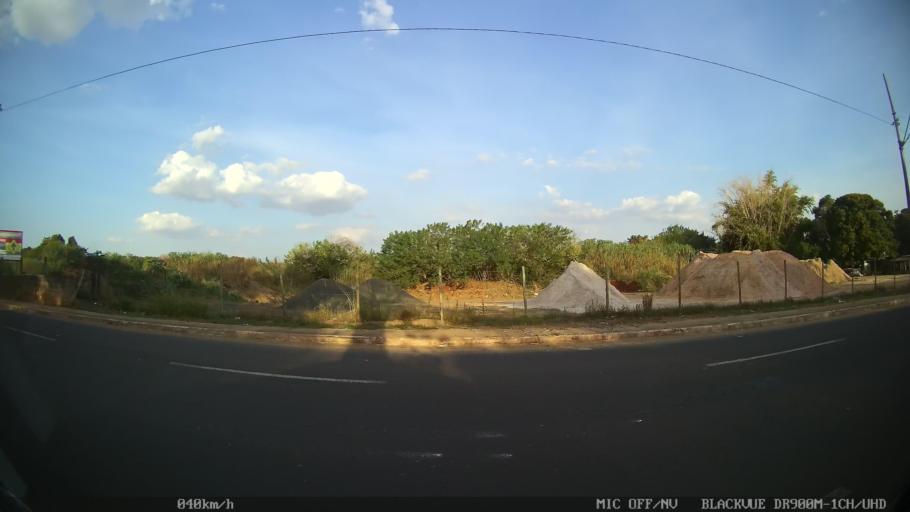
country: BR
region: Sao Paulo
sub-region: Ribeirao Preto
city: Ribeirao Preto
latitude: -21.1453
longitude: -47.8029
